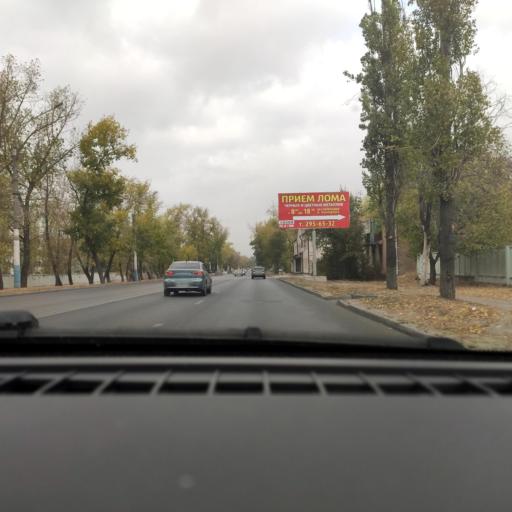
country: RU
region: Voronezj
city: Somovo
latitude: 51.7113
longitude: 39.2760
